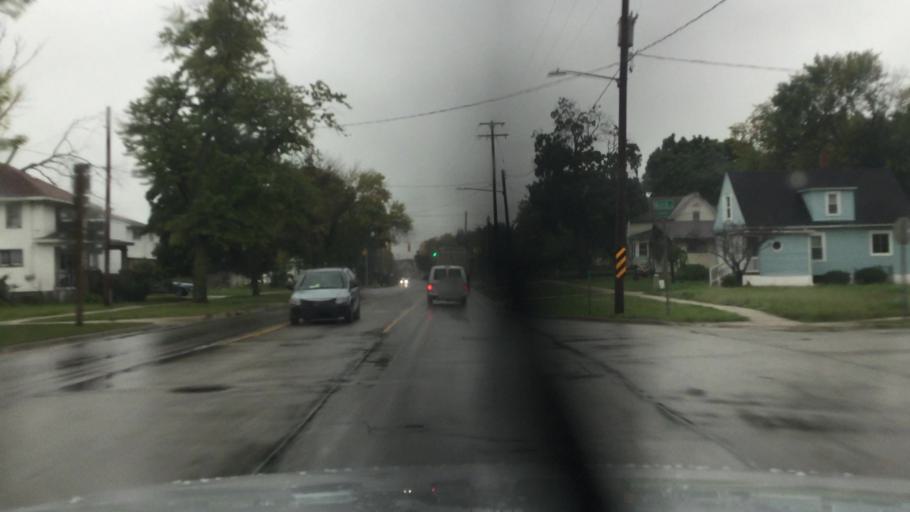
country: US
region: Michigan
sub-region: Saginaw County
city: Saginaw
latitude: 43.4089
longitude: -83.9556
